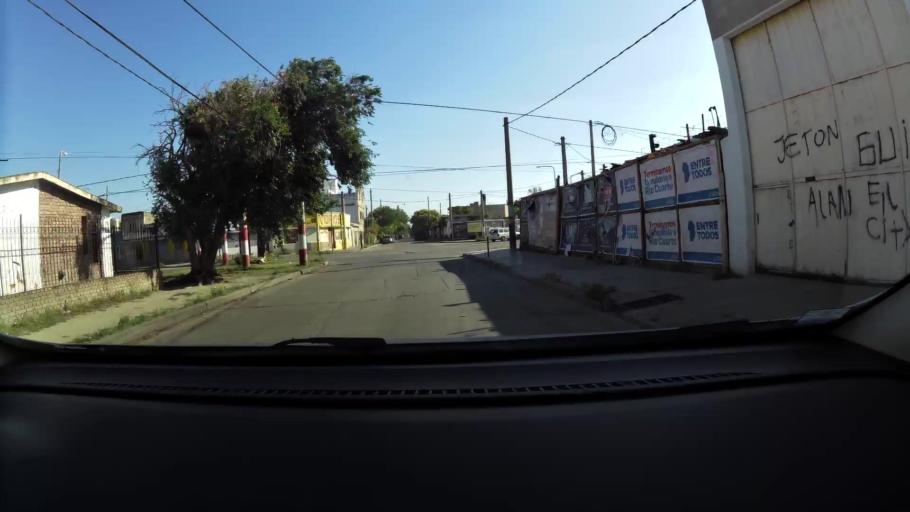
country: AR
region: Cordoba
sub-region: Departamento de Capital
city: Cordoba
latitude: -31.3874
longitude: -64.1660
